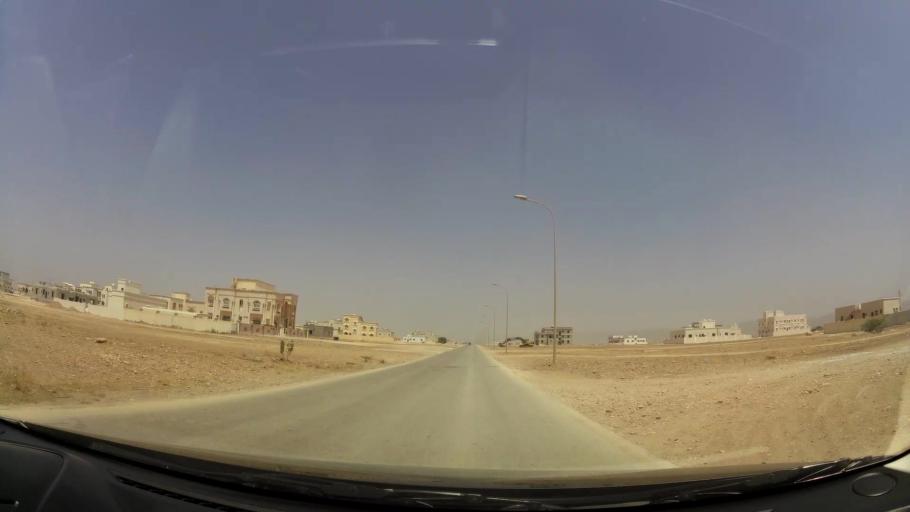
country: OM
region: Zufar
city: Salalah
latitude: 17.0920
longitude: 54.2136
